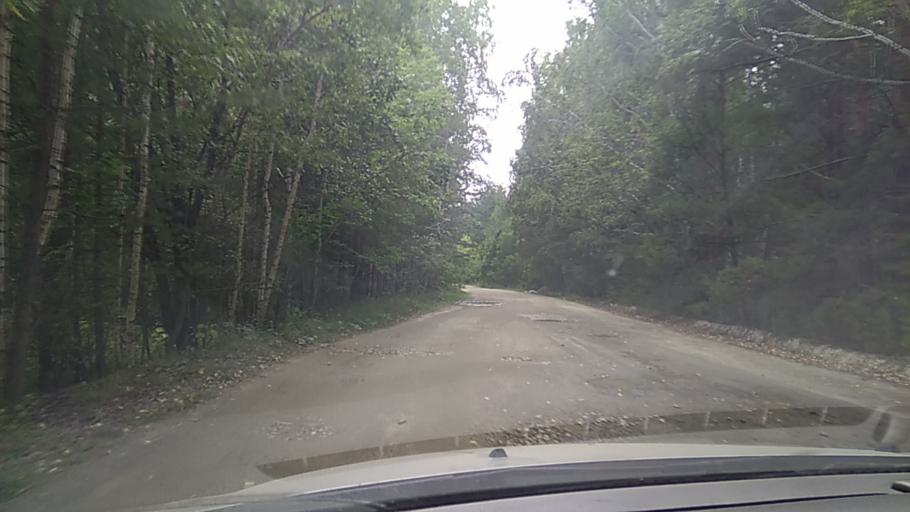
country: RU
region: Chelyabinsk
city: Kyshtym
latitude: 55.6786
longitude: 60.5828
